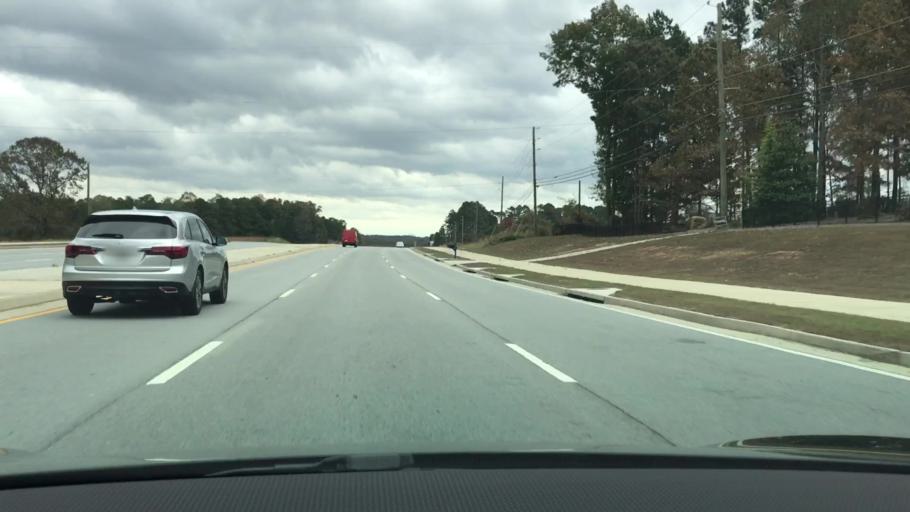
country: US
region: Georgia
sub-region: Hall County
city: Flowery Branch
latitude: 34.1163
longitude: -83.9073
